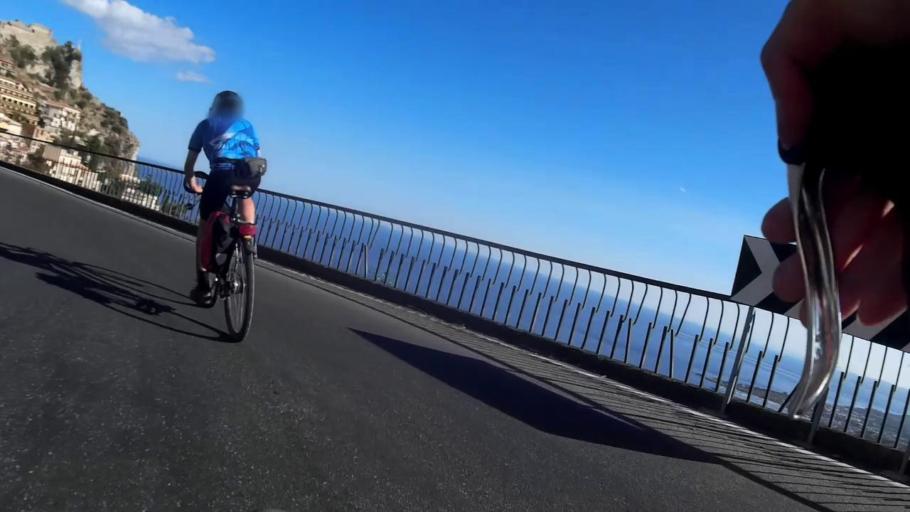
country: IT
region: Sicily
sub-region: Messina
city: Castelmola
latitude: 37.8550
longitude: 15.2805
